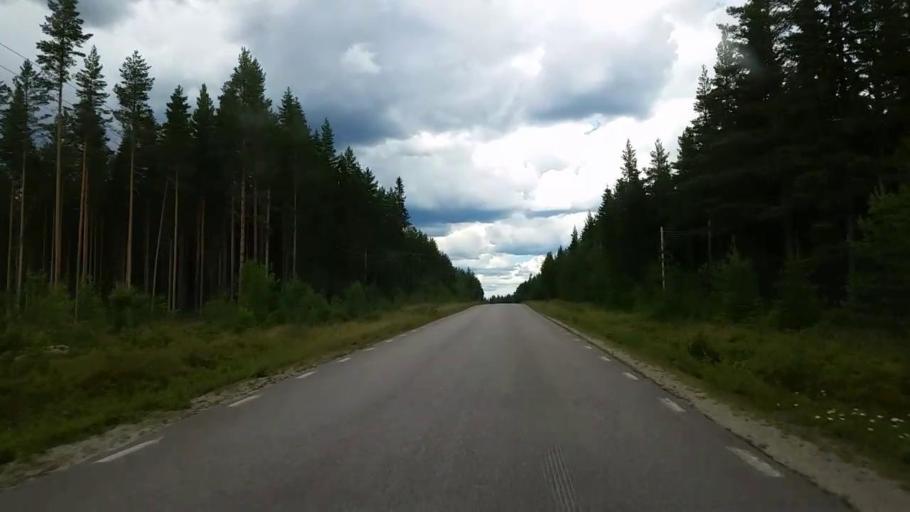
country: SE
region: Gaevleborg
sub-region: Ovanakers Kommun
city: Edsbyn
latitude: 61.4263
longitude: 15.8994
